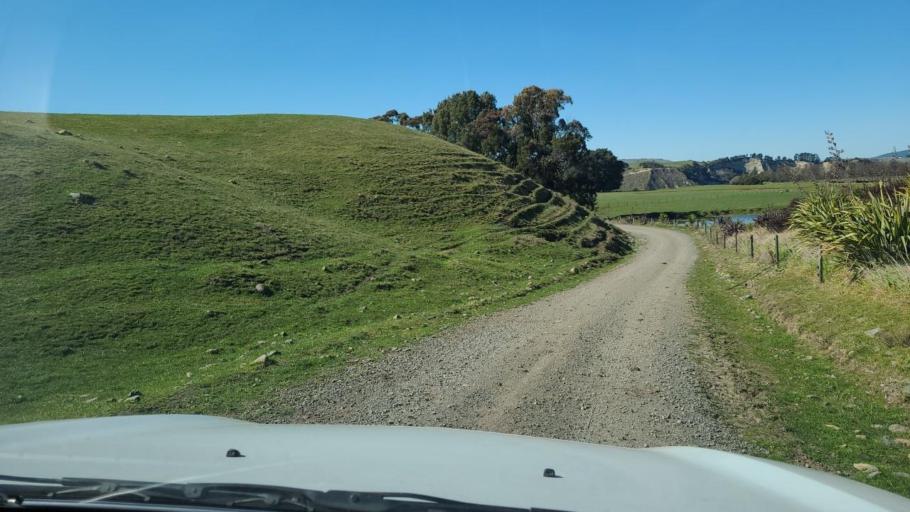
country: NZ
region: Hawke's Bay
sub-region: Napier City
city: Taradale
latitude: -39.4343
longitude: 176.5594
